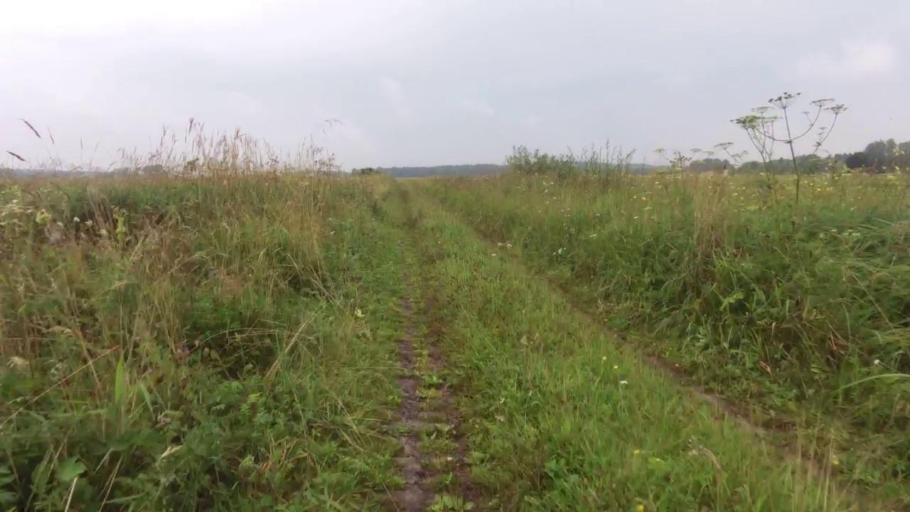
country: PL
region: West Pomeranian Voivodeship
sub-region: Powiat stargardzki
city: Suchan
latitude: 53.2511
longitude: 15.3984
